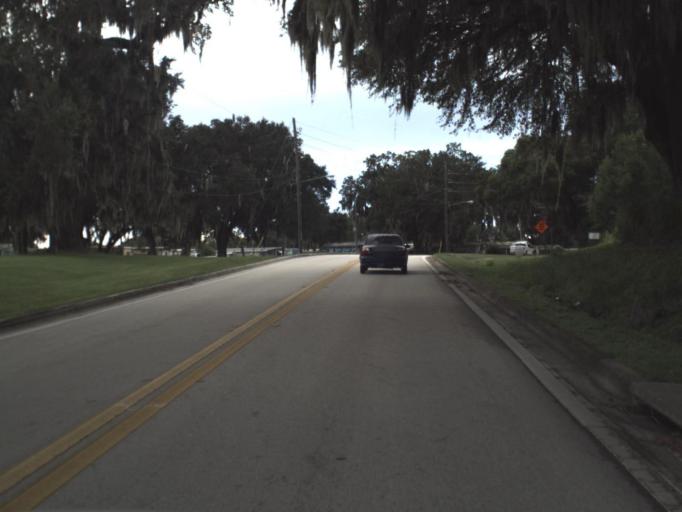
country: US
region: Florida
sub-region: Polk County
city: Fort Meade
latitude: 27.7515
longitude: -81.7833
